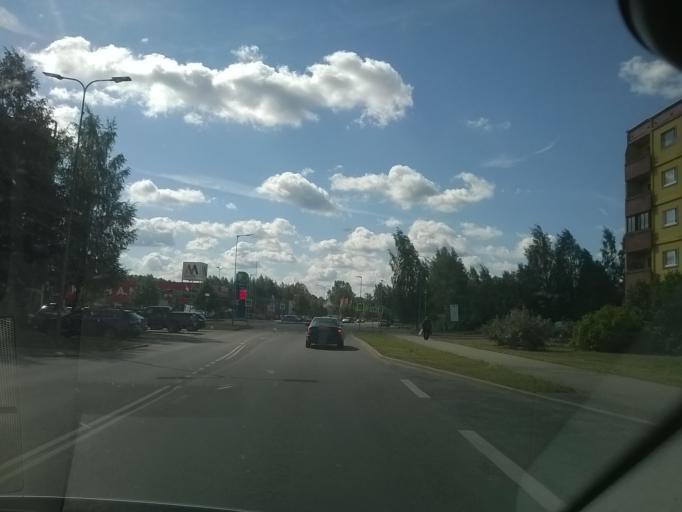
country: EE
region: Vorumaa
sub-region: Voru linn
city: Voru
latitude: 57.8369
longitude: 27.0087
